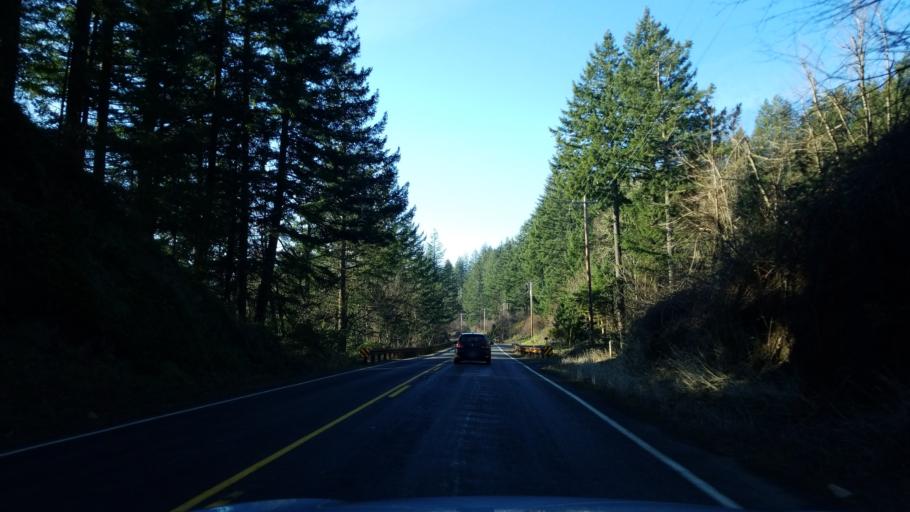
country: US
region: Oregon
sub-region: Hood River County
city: Cascade Locks
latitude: 45.6052
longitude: -122.0927
